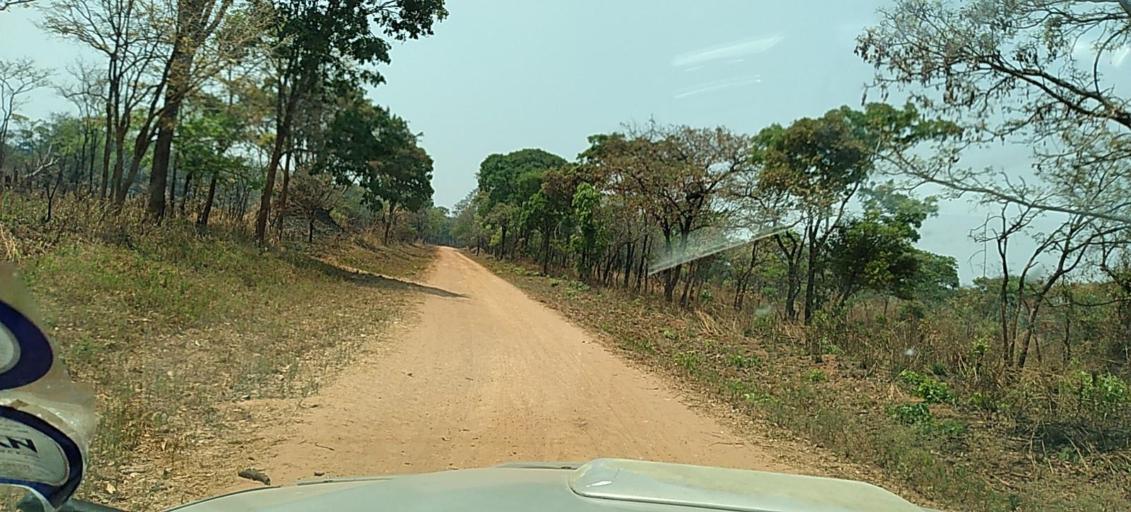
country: ZM
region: North-Western
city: Kasempa
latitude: -13.5447
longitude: 26.0438
